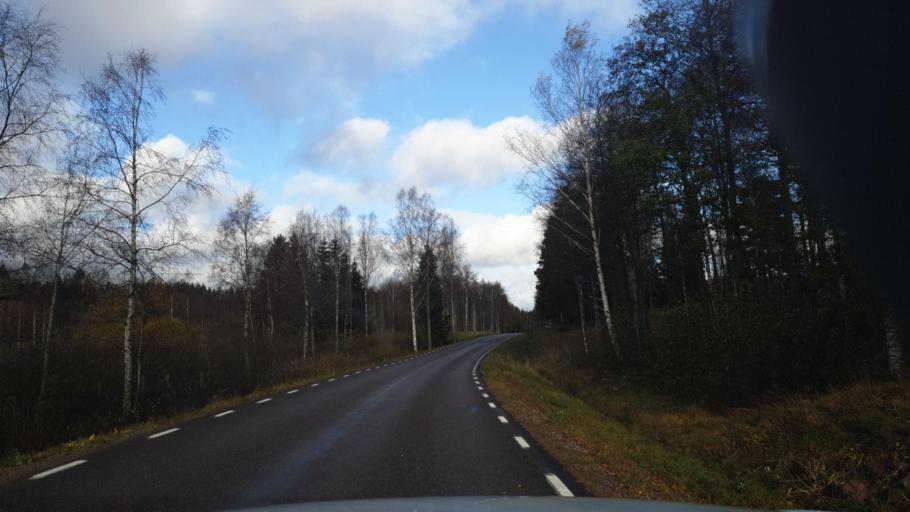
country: SE
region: Vaermland
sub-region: Grums Kommun
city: Slottsbron
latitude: 59.4804
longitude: 12.8840
